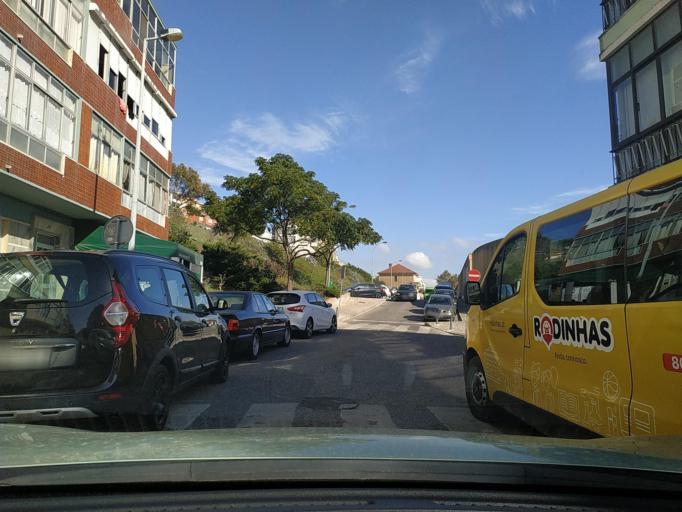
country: PT
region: Lisbon
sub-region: Amadora
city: Amadora
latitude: 38.7640
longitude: -9.2362
